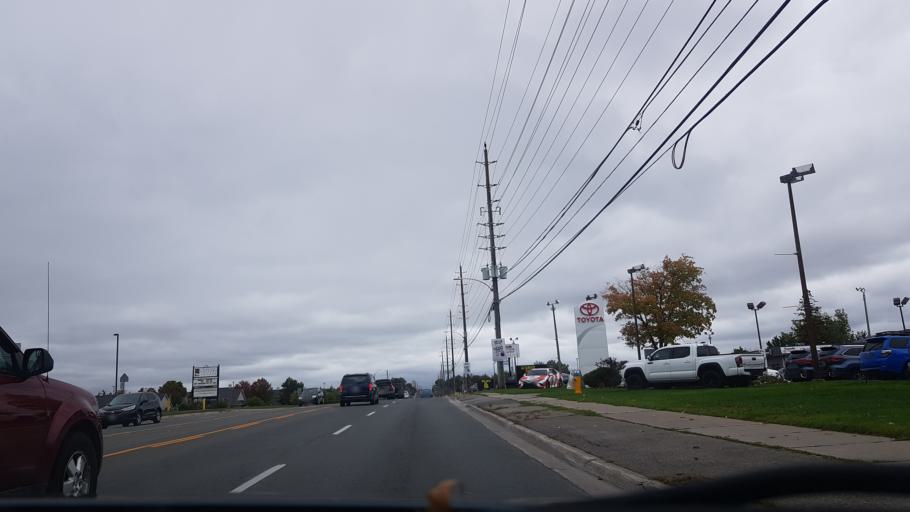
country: CA
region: Ontario
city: Peterborough
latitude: 44.2790
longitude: -78.3577
